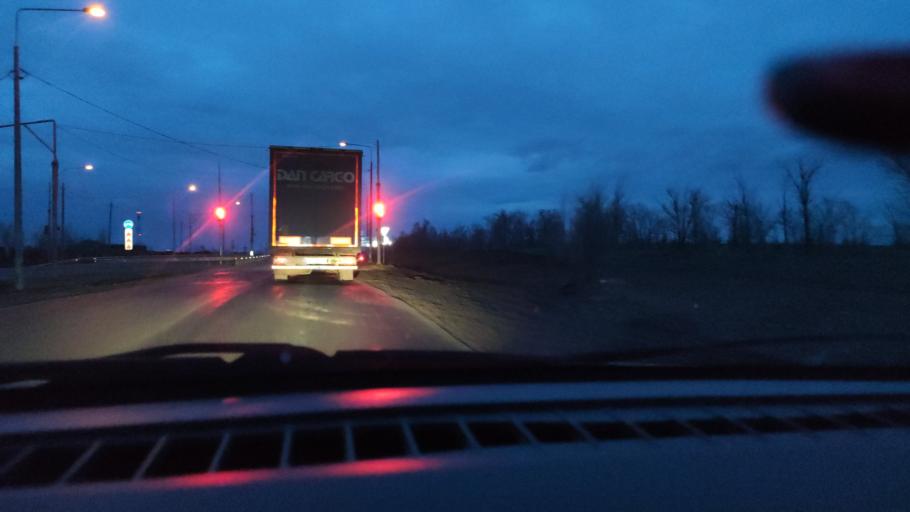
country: RU
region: Orenburg
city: Tatarskaya Kargala
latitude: 51.9699
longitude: 55.1857
